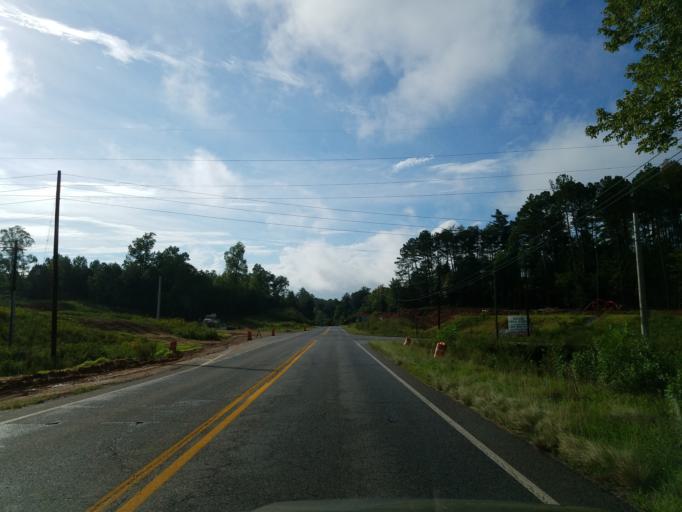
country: US
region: Georgia
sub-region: White County
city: Cleveland
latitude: 34.6103
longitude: -83.7744
